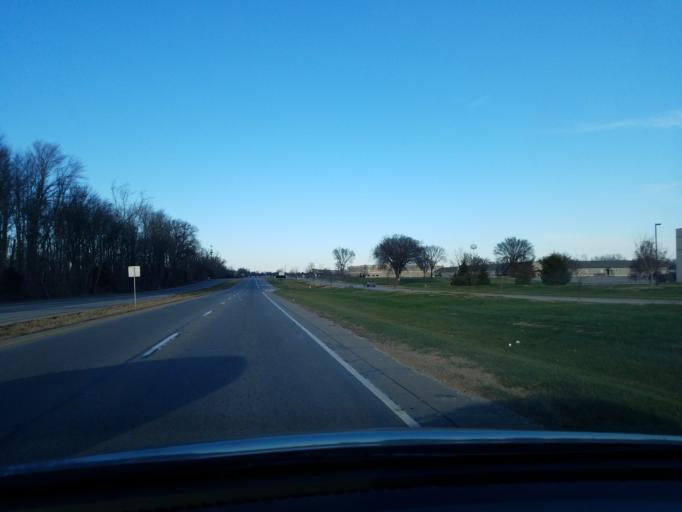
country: US
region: Indiana
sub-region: Clark County
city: Oak Park
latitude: 38.3615
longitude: -85.7001
